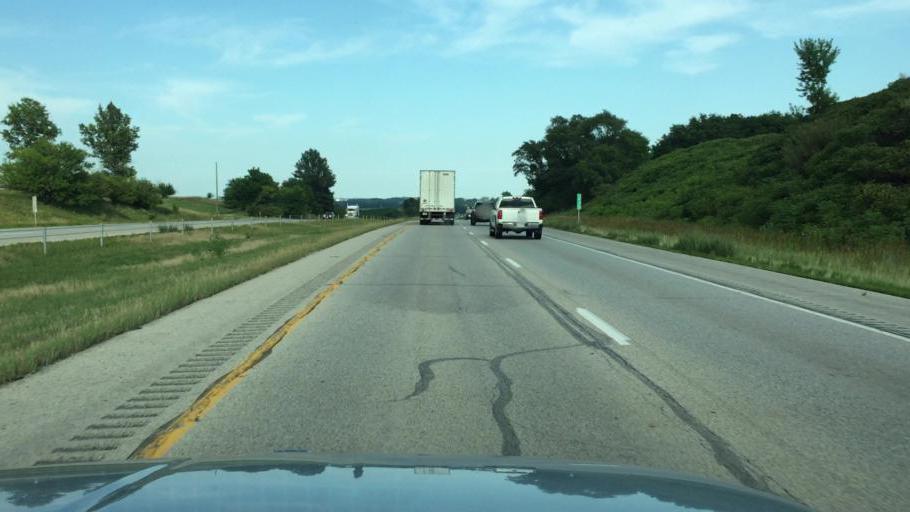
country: US
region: Iowa
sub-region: Johnson County
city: Tiffin
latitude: 41.6952
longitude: -91.7185
